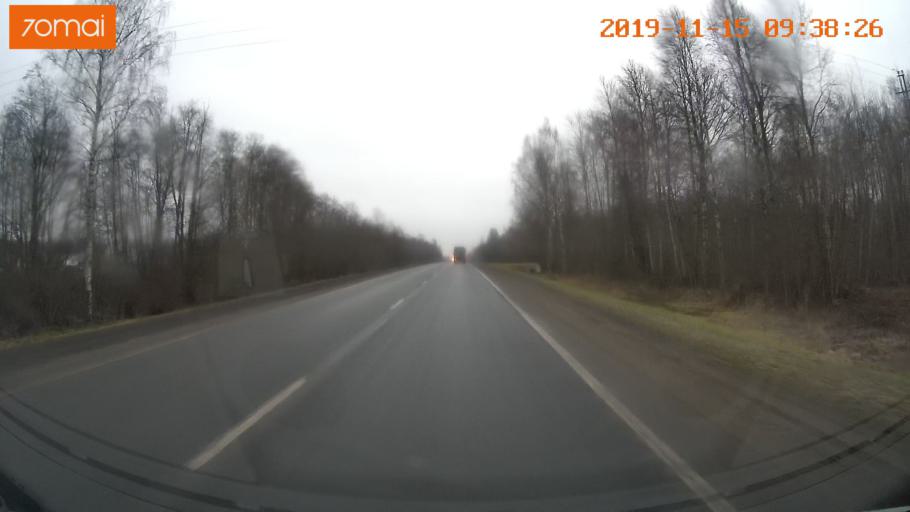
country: RU
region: Vologda
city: Sheksna
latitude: 59.2319
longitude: 38.4556
